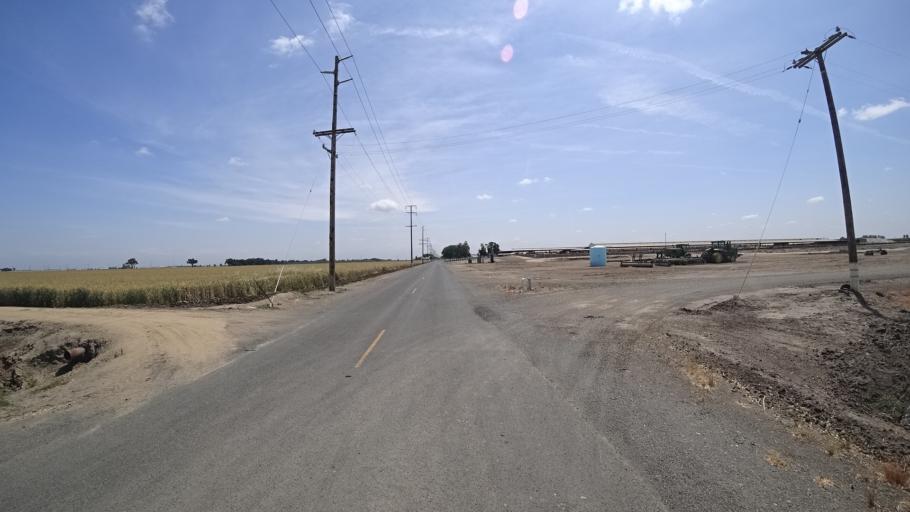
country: US
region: California
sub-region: Tulare County
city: Goshen
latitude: 36.2835
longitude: -119.4835
